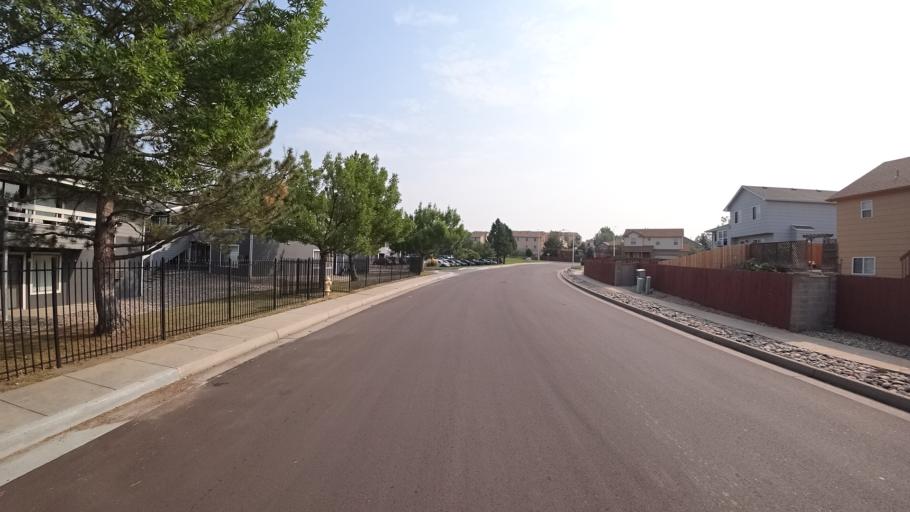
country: US
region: Colorado
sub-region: El Paso County
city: Stratmoor
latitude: 38.8215
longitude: -104.7518
